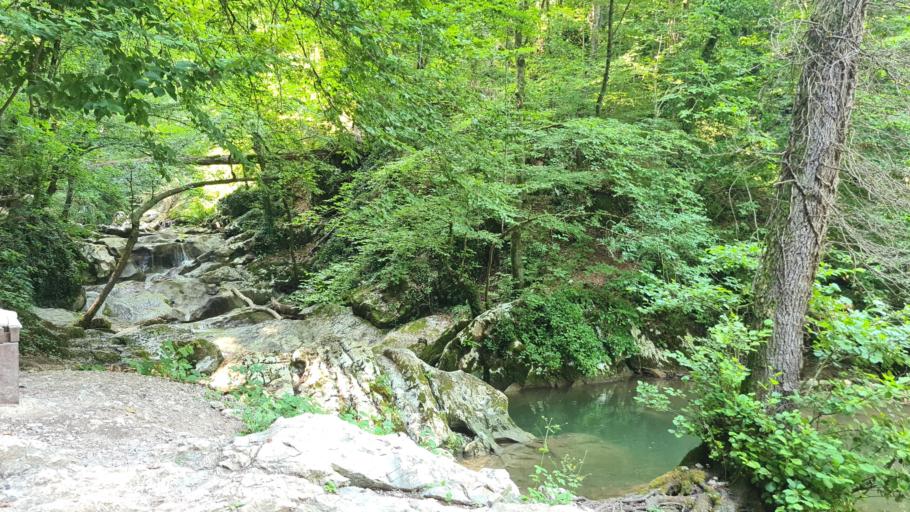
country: SI
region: Skocjan
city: Skocjan
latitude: 45.9063
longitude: 15.2331
